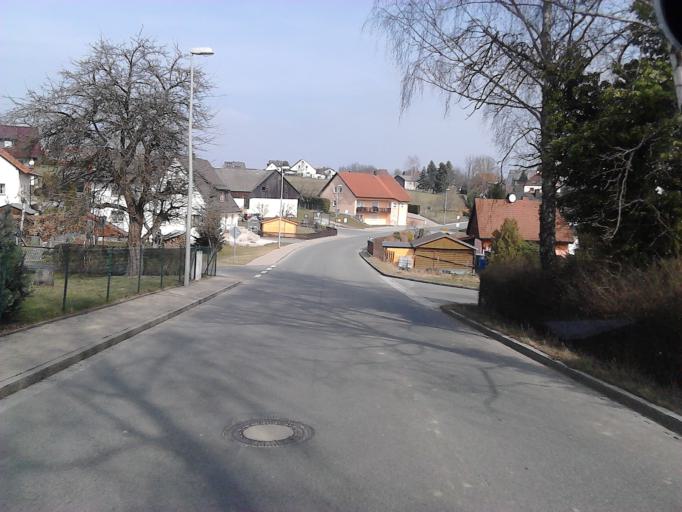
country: DE
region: Bavaria
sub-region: Upper Franconia
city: Pottenstein
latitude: 49.7291
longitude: 11.3973
